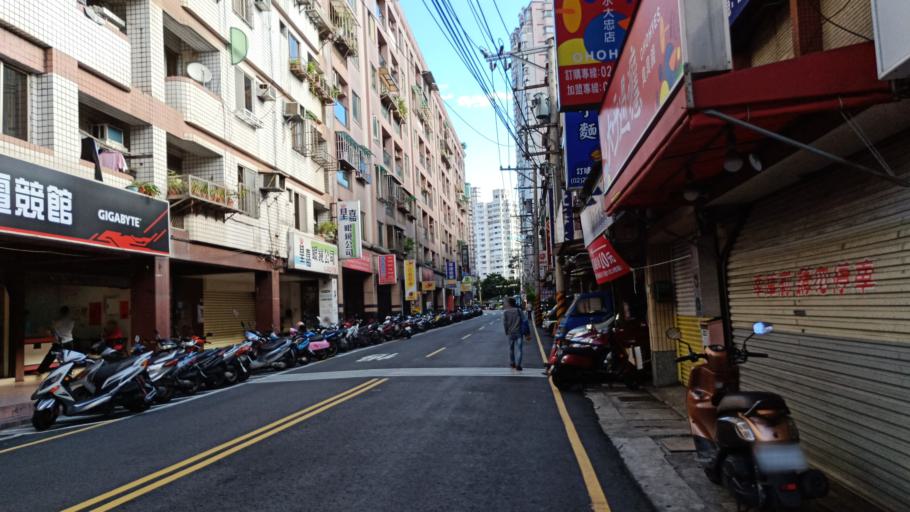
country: TW
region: Taipei
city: Taipei
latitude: 25.1759
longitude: 121.4435
